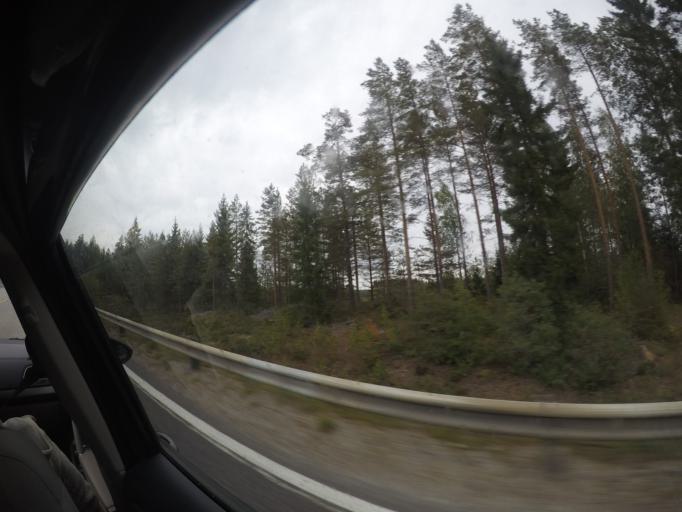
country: FI
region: Pirkanmaa
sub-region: Ylae-Pirkanmaa
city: Juupajoki
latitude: 61.7684
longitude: 24.3073
